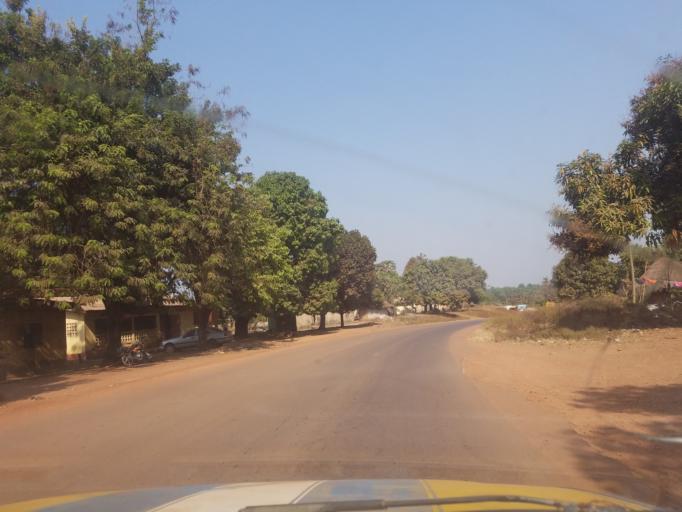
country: GN
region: Boke
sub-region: Boke Prefecture
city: Boke
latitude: 10.8339
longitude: -14.3649
